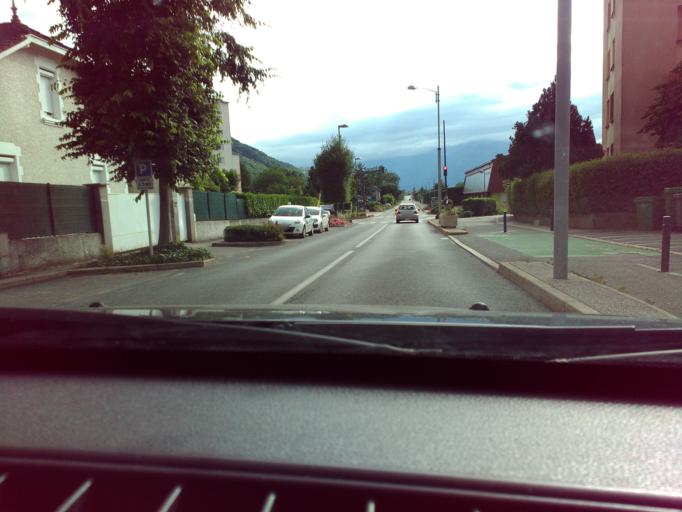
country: FR
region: Rhone-Alpes
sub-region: Departement de l'Isere
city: Domene
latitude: 45.1968
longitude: 5.8301
